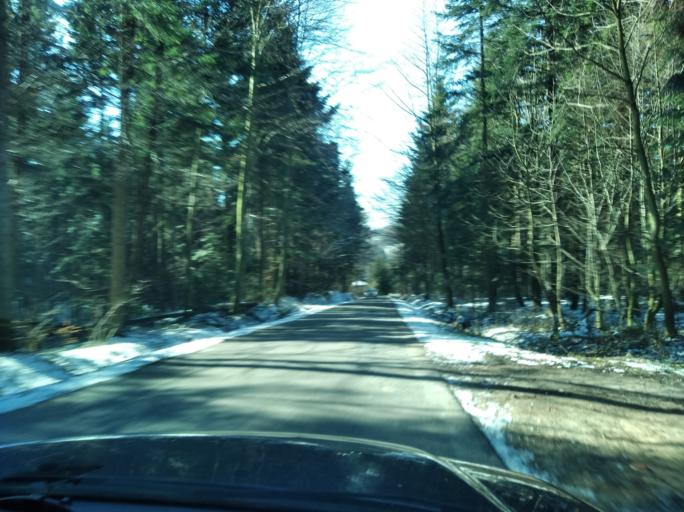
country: PL
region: Subcarpathian Voivodeship
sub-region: Powiat strzyzowski
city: Jawornik
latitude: 49.8610
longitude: 21.8683
